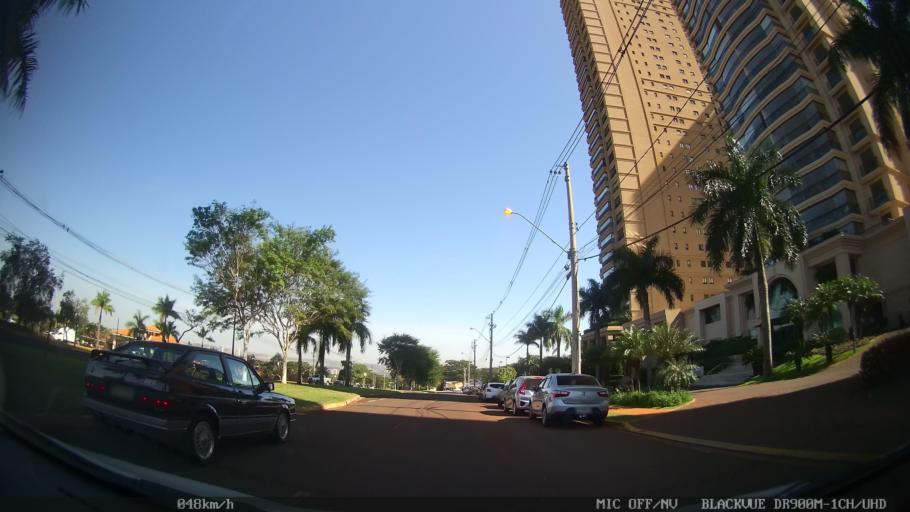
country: BR
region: Sao Paulo
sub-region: Ribeirao Preto
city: Ribeirao Preto
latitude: -21.2194
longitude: -47.8042
